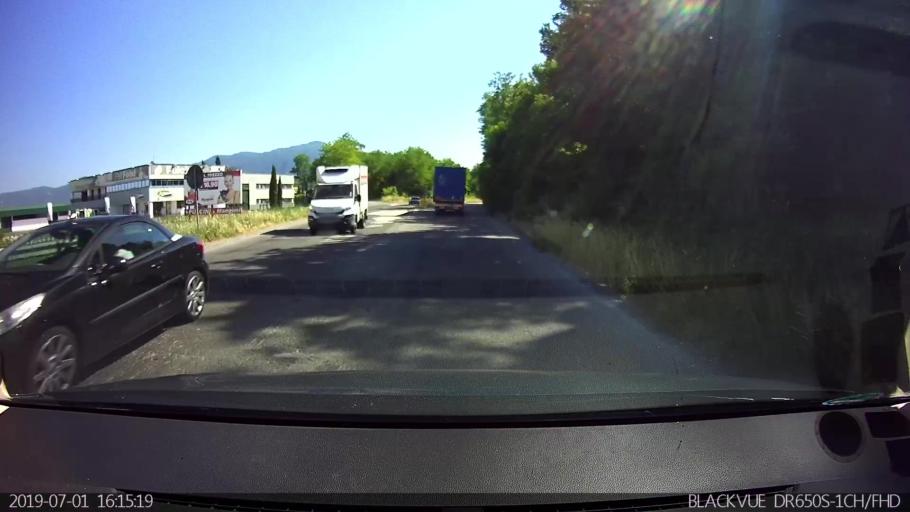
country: IT
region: Latium
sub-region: Provincia di Frosinone
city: Ceccano
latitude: 41.5937
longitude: 13.2911
